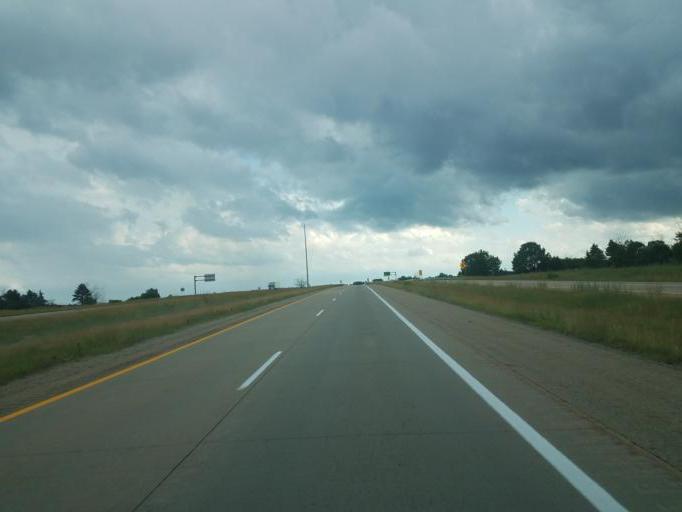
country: US
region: Michigan
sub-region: Calhoun County
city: Marshall
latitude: 42.2999
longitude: -84.9966
